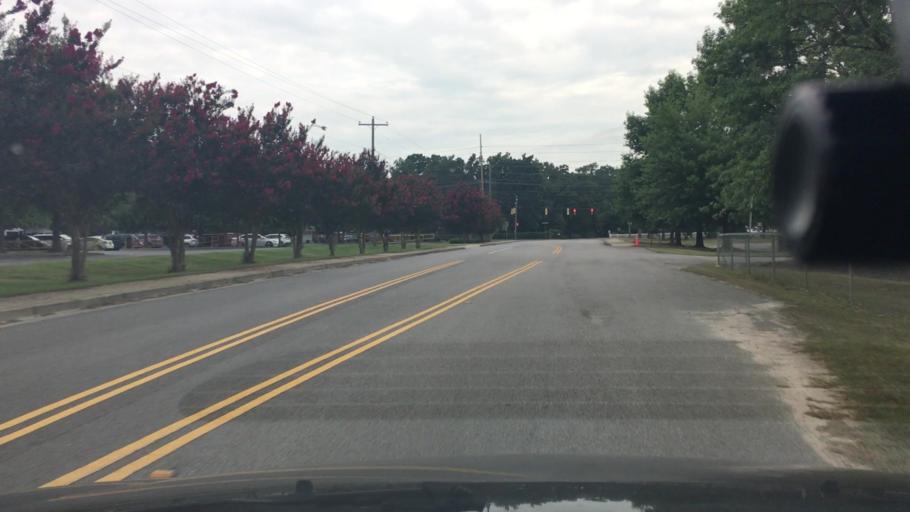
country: US
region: South Carolina
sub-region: Aiken County
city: Aiken
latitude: 33.5237
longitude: -81.7150
